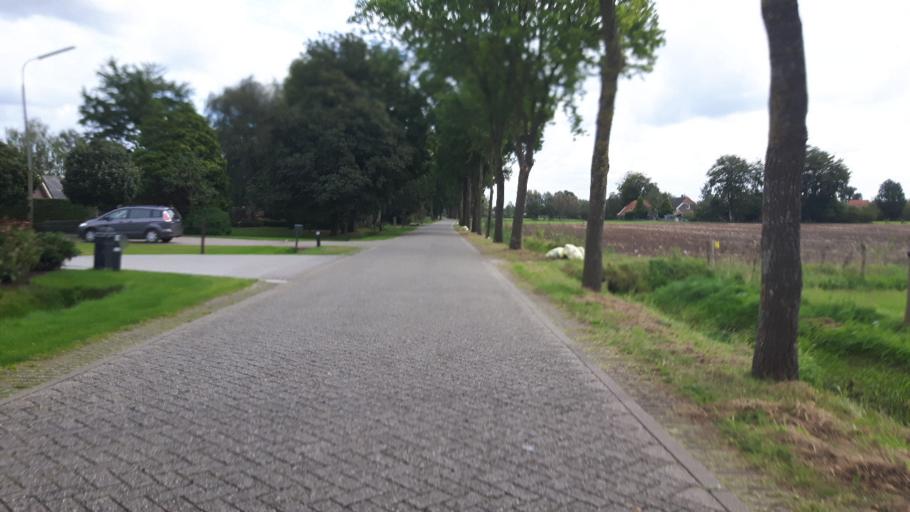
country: NL
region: Gelderland
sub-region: Gemeente Putten
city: Putten
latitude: 52.2556
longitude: 5.5531
